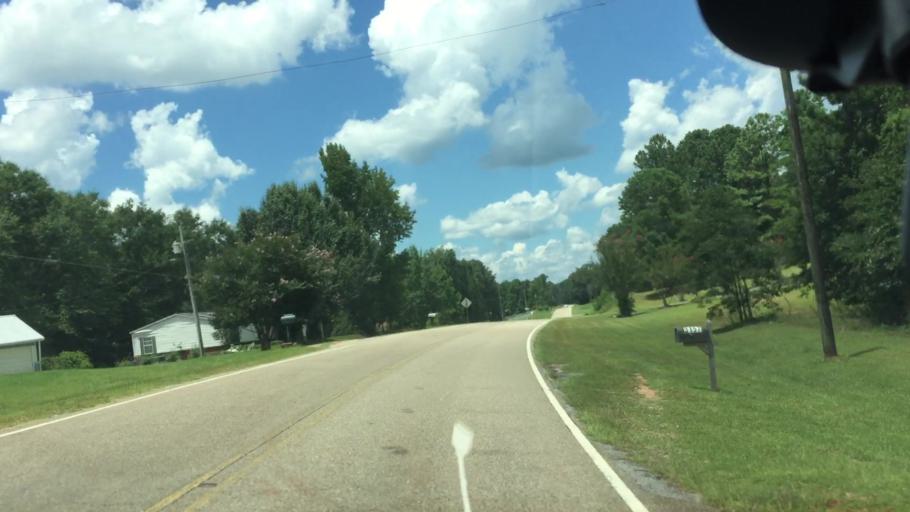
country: US
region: Alabama
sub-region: Coffee County
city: Enterprise
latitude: 31.4013
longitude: -85.8375
